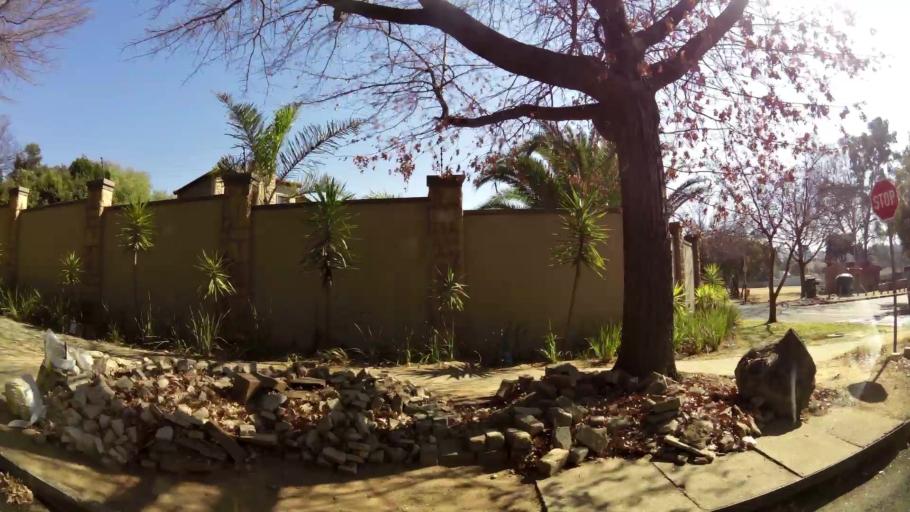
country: ZA
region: Gauteng
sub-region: City of Johannesburg Metropolitan Municipality
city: Modderfontein
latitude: -26.1587
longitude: 28.1239
